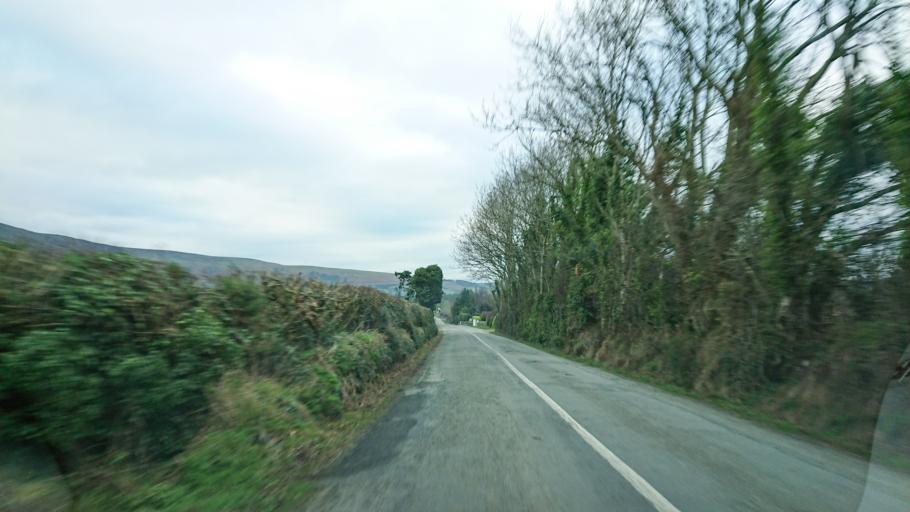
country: IE
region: Munster
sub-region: South Tipperary
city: Cluain Meala
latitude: 52.3214
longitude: -7.5662
